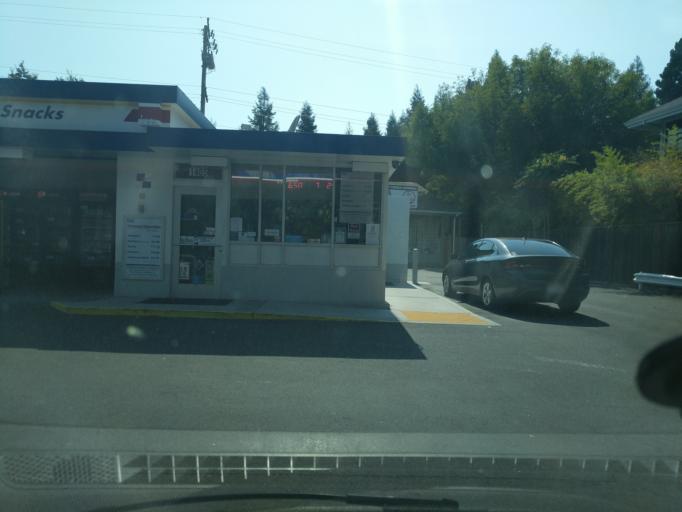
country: US
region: California
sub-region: Contra Costa County
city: Alamo
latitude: 37.8476
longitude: -122.0312
